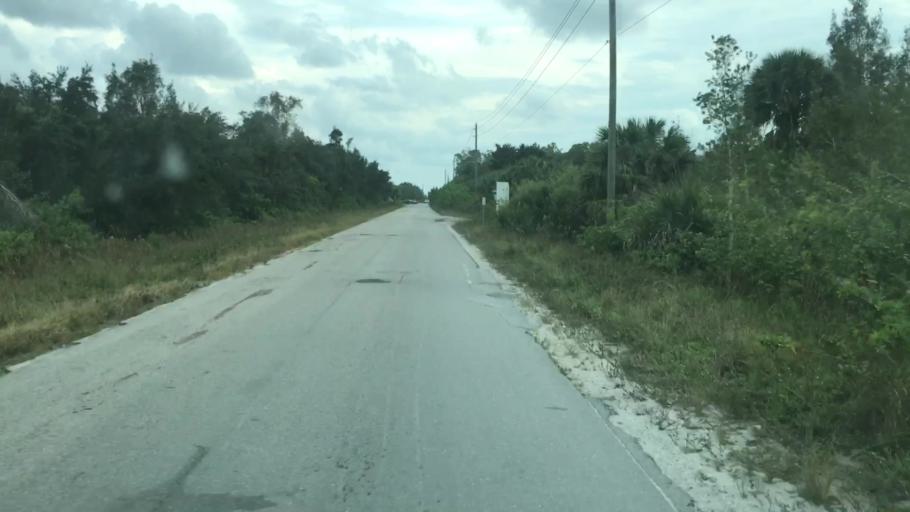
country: US
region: Florida
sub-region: Lee County
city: Bonita Springs
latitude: 26.3557
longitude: -81.7388
